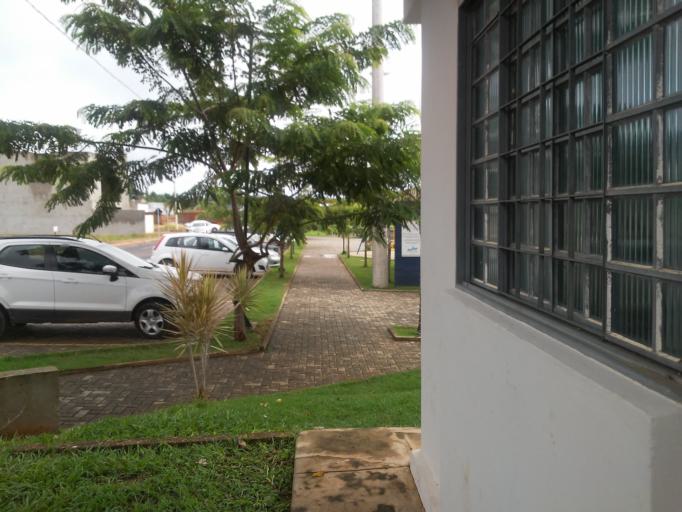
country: BR
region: Goias
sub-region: Ipameri
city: Ipameri
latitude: -17.7199
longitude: -48.1671
